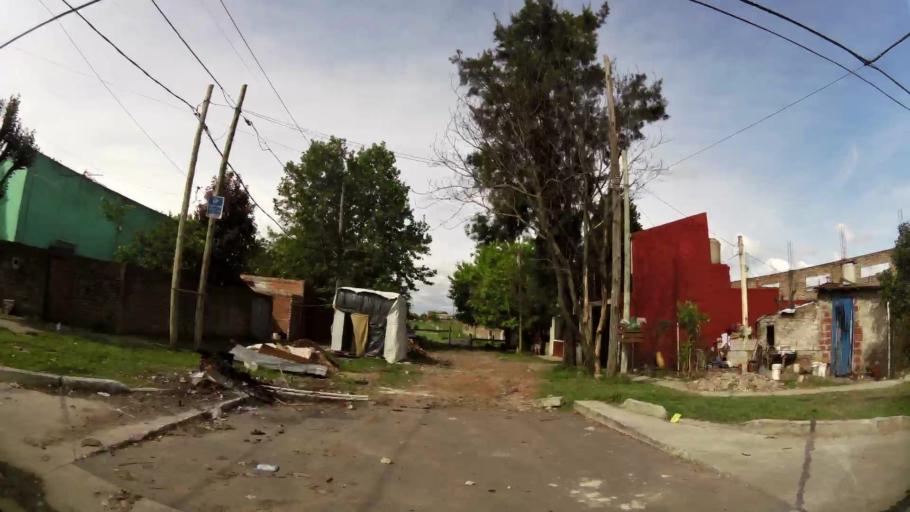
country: AR
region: Buenos Aires
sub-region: Partido de Quilmes
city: Quilmes
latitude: -34.7742
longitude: -58.2587
